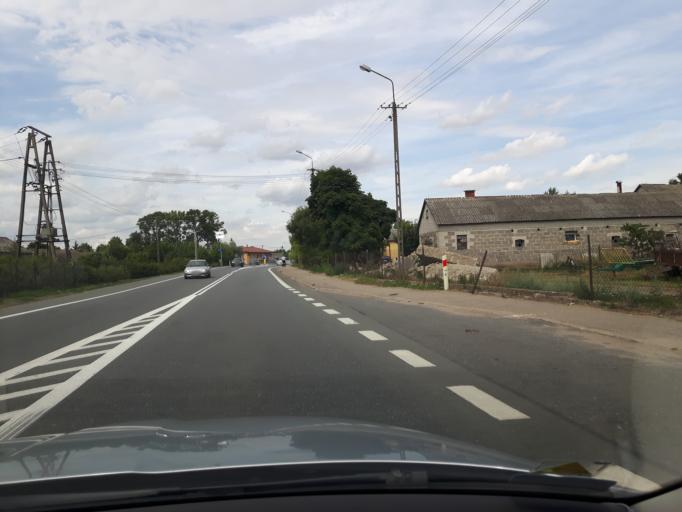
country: PL
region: Masovian Voivodeship
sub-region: Powiat mlawski
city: Strzegowo
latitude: 52.9414
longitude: 20.2823
